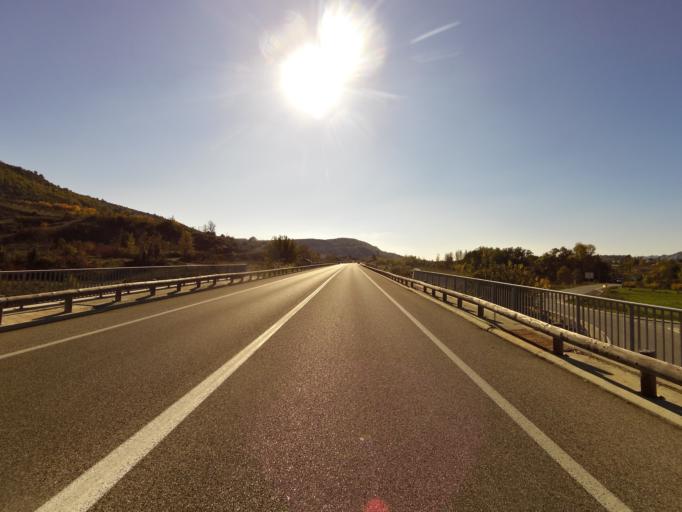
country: FR
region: Rhone-Alpes
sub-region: Departement de l'Ardeche
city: Lachapelle-sous-Aubenas
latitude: 44.5707
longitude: 4.3757
